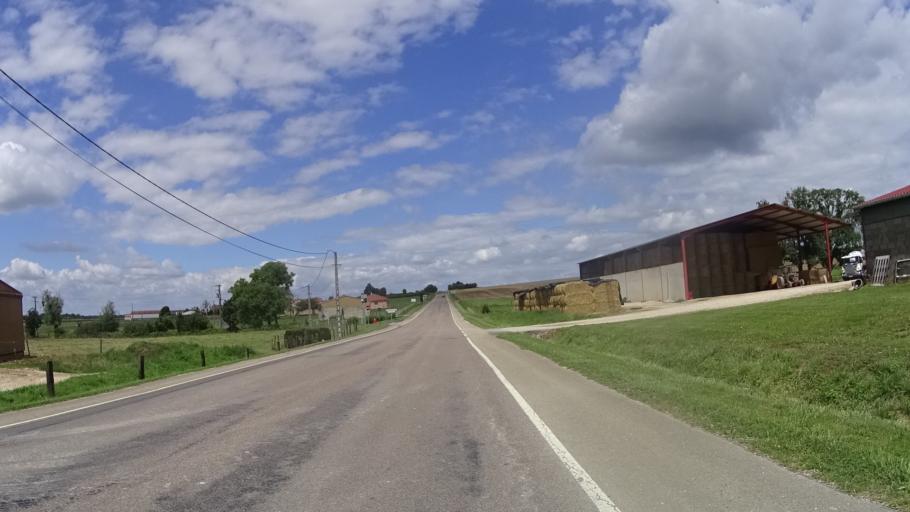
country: FR
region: Champagne-Ardenne
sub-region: Departement de la Haute-Marne
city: Montier-en-Der
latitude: 48.4873
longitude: 4.7595
